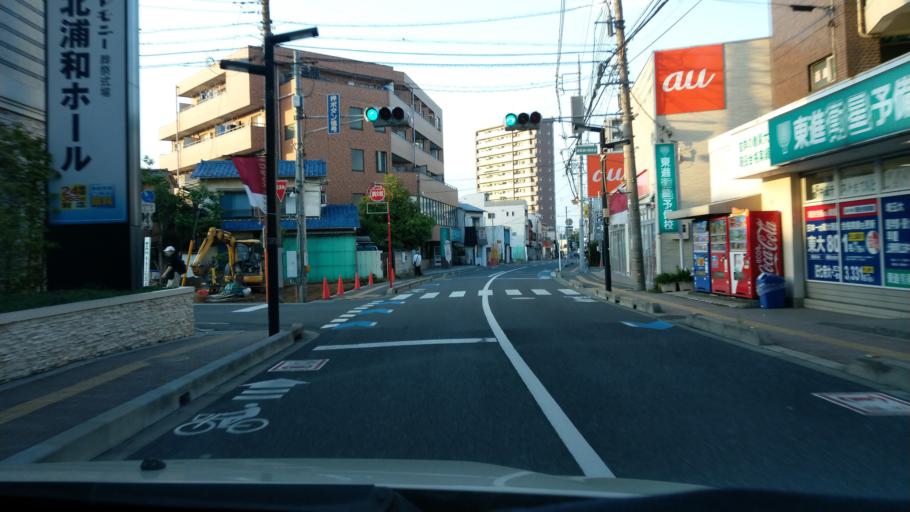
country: JP
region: Saitama
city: Yono
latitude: 35.8751
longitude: 139.6487
